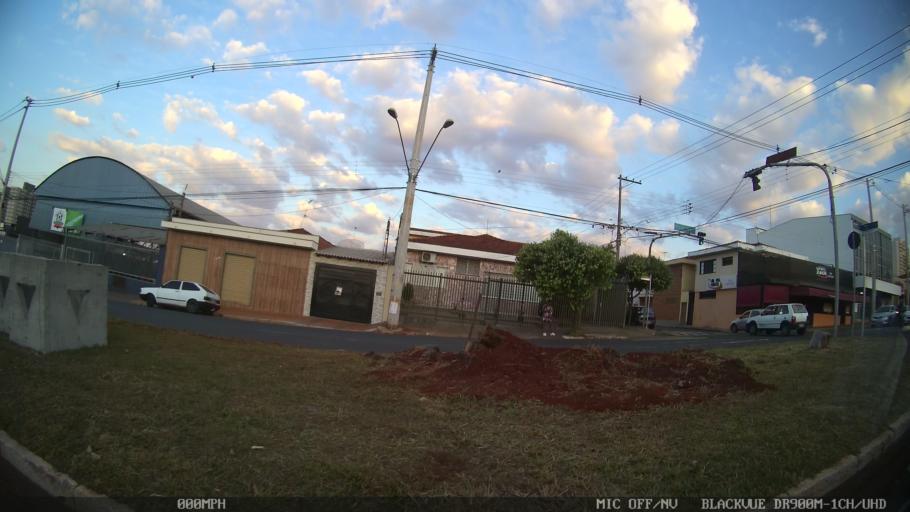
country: BR
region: Sao Paulo
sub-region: Ribeirao Preto
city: Ribeirao Preto
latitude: -21.1706
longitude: -47.7923
